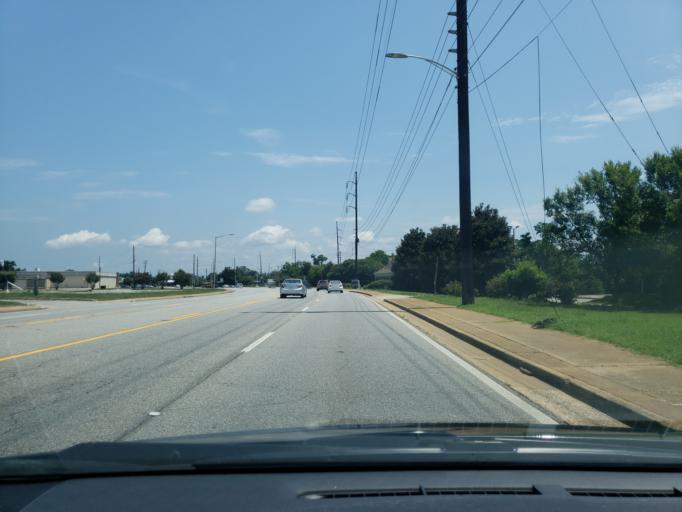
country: US
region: Georgia
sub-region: Dougherty County
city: Albany
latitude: 31.5795
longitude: -84.1796
